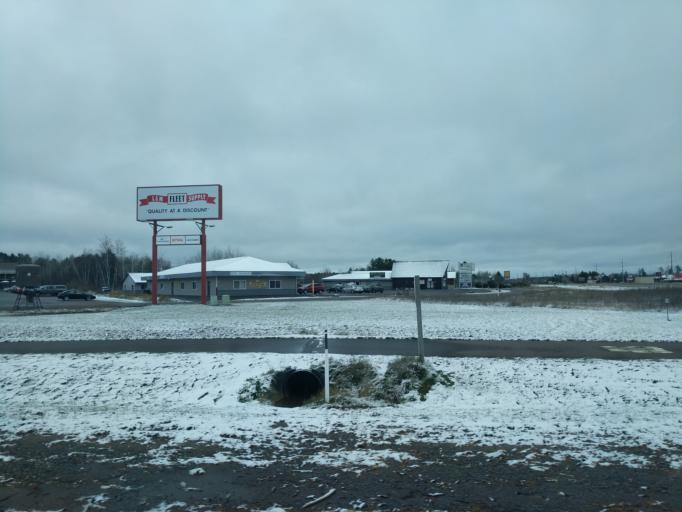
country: US
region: Wisconsin
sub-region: Sawyer County
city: Hayward
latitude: 46.0192
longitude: -91.4765
